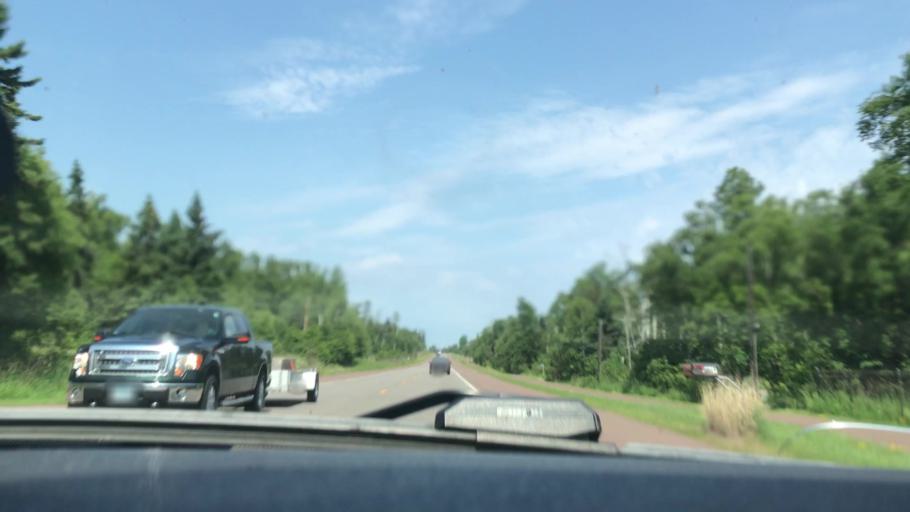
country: US
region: Minnesota
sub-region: Cook County
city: Grand Marais
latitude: 47.5889
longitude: -90.8077
